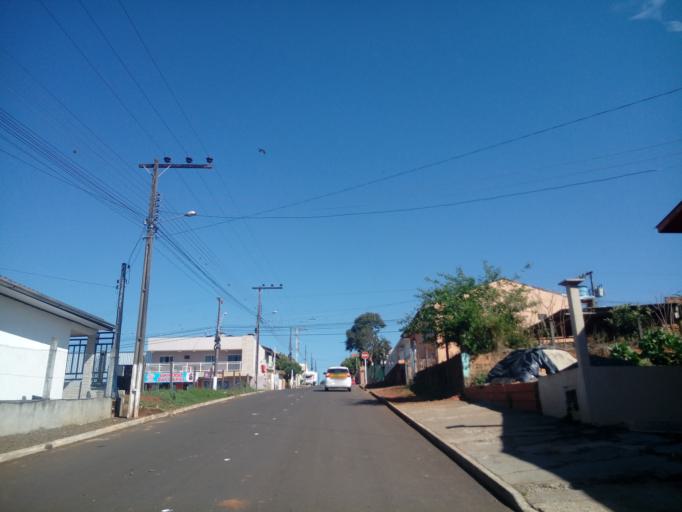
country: BR
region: Santa Catarina
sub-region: Chapeco
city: Chapeco
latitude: -27.0935
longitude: -52.6734
